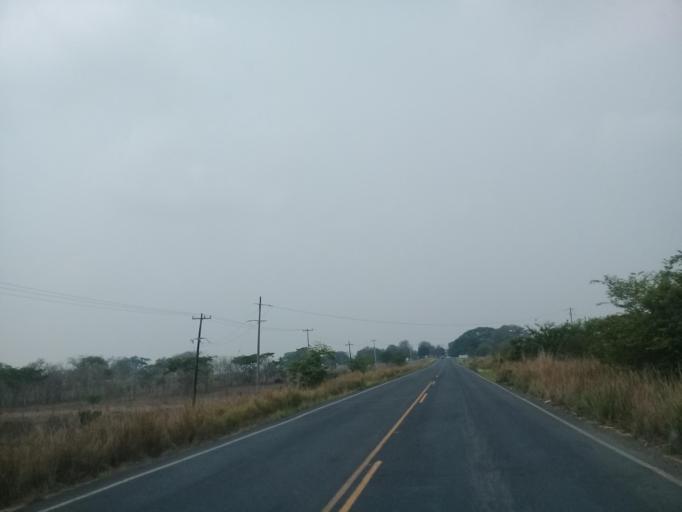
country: MX
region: Veracruz
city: Jamapa
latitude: 18.9150
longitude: -96.1988
